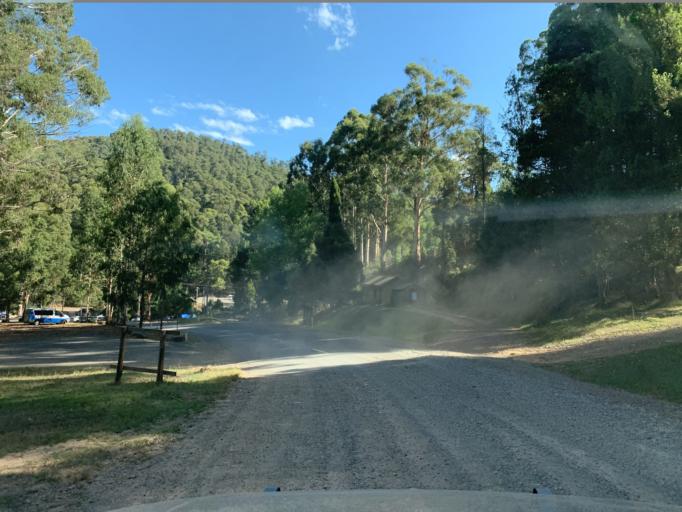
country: AU
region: Victoria
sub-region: Mansfield
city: Mansfield
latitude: -37.1077
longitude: 146.3995
